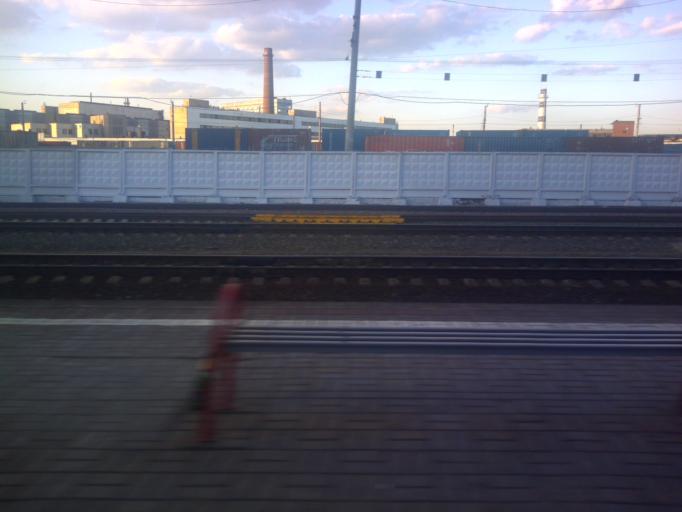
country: RU
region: Moscow
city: Lefortovo
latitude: 55.7449
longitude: 37.6900
